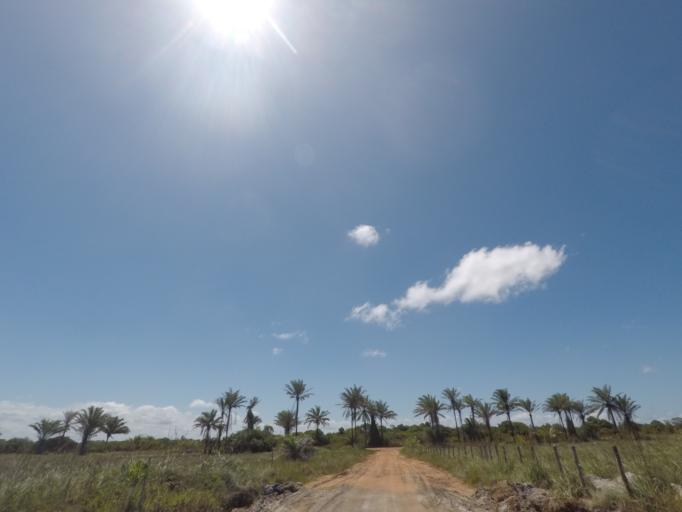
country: BR
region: Bahia
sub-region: Marau
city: Marau
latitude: -13.9672
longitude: -38.9466
